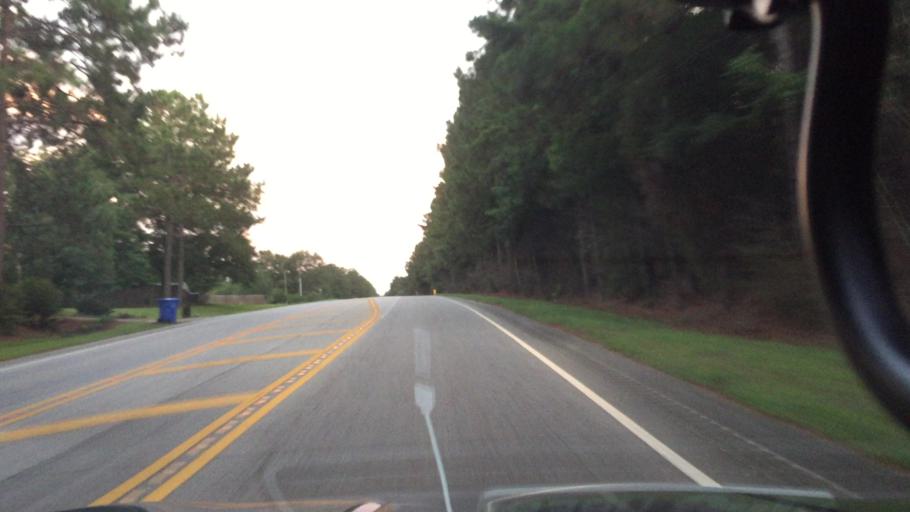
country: US
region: Alabama
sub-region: Coffee County
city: New Brockton
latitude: 31.3954
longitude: -85.8790
